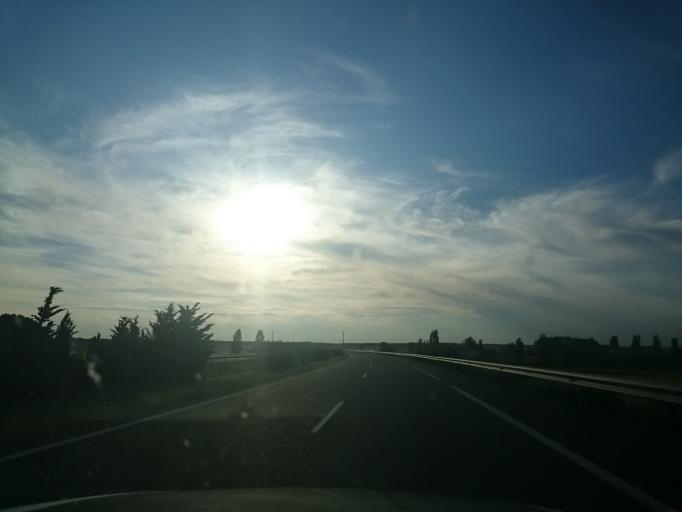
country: ES
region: Castille and Leon
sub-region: Provincia de Leon
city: Sahagun
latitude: 42.3731
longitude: -4.9922
